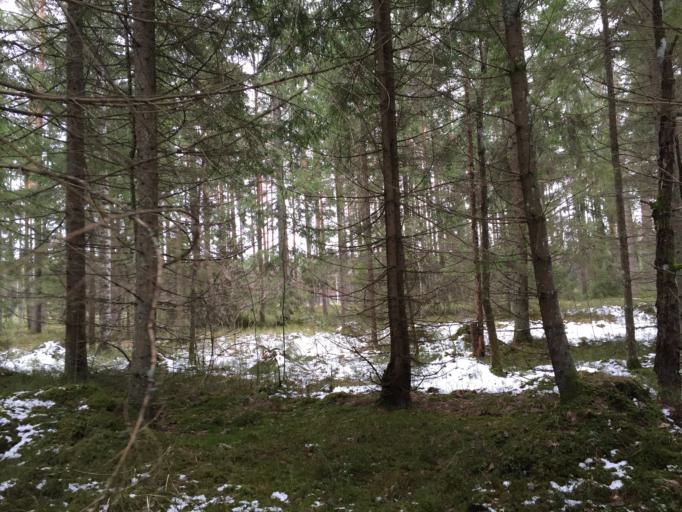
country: LV
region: Garkalne
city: Garkalne
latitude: 56.9656
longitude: 24.4742
